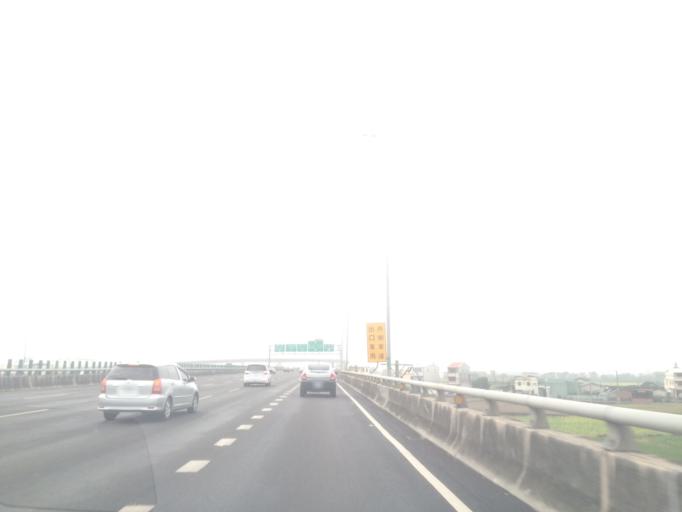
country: TW
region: Taiwan
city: Zhongxing New Village
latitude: 24.0322
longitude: 120.6721
